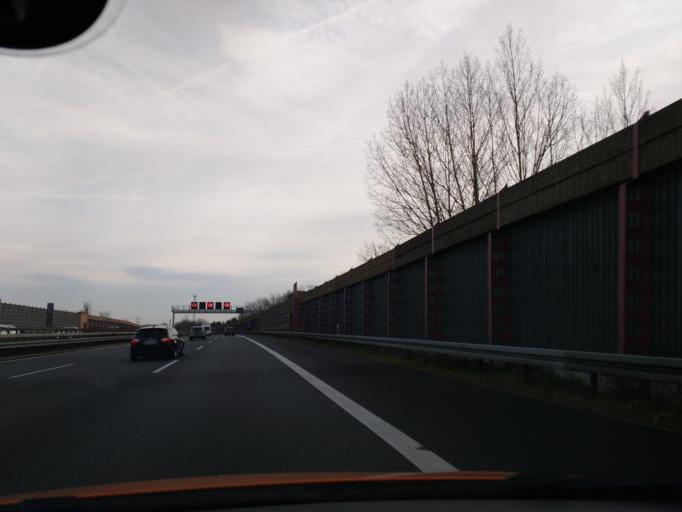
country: DE
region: Lower Saxony
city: Peine
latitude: 52.3401
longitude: 10.2238
